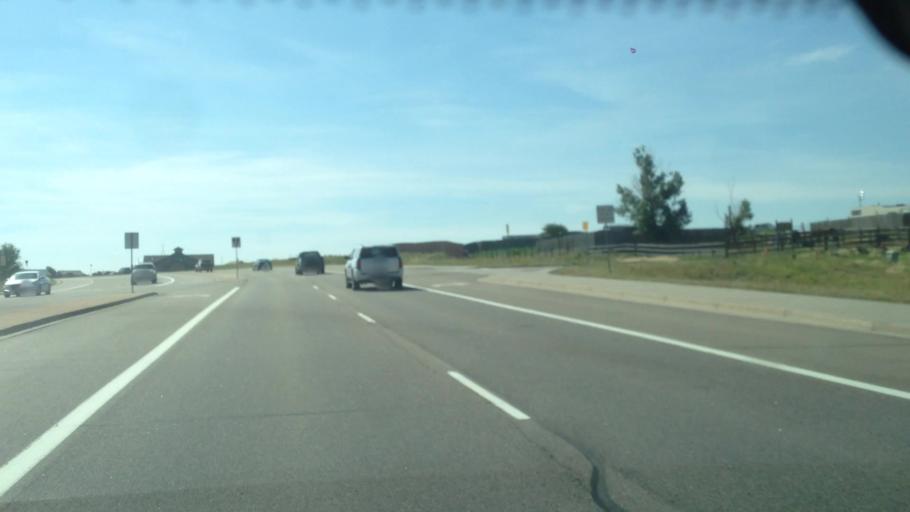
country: US
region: Colorado
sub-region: Douglas County
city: Stonegate
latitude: 39.5161
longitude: -104.8095
